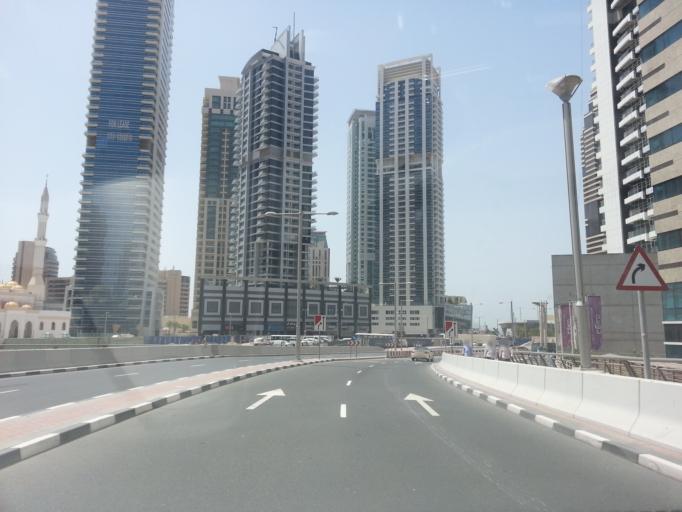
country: AE
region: Dubai
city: Dubai
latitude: 25.0829
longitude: 55.1440
